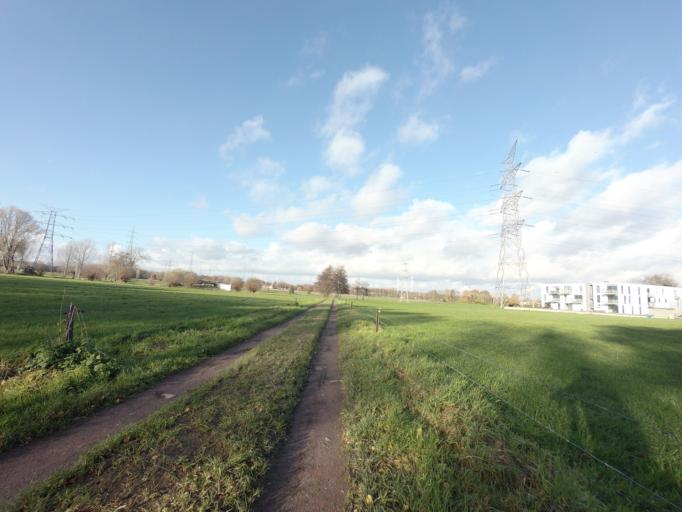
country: BE
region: Flanders
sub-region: Provincie Antwerpen
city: Niel
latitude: 51.1129
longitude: 4.3219
